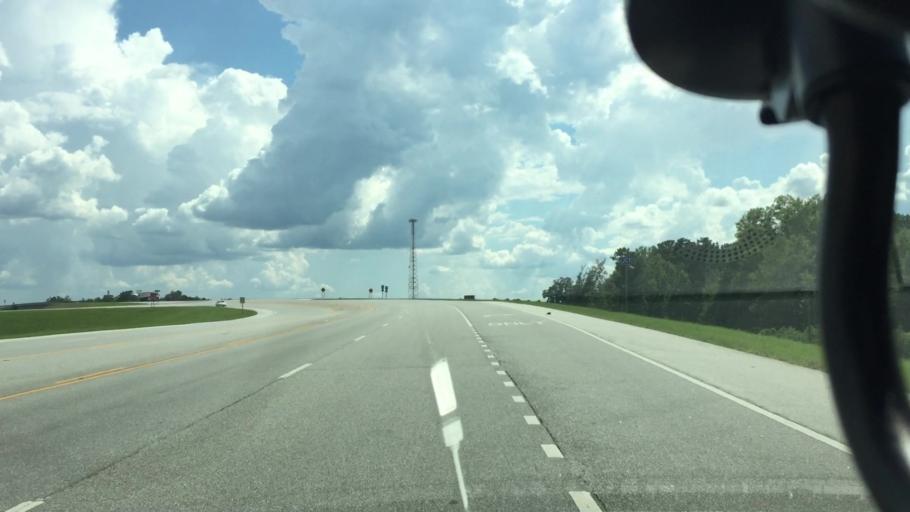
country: US
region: Alabama
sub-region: Lee County
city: Auburn
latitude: 32.5513
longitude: -85.5291
